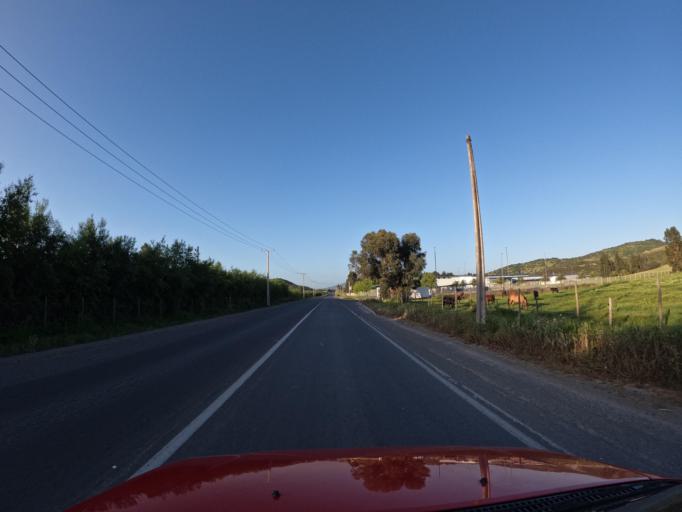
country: CL
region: O'Higgins
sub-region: Provincia de Colchagua
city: Santa Cruz
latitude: -34.3262
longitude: -71.3928
